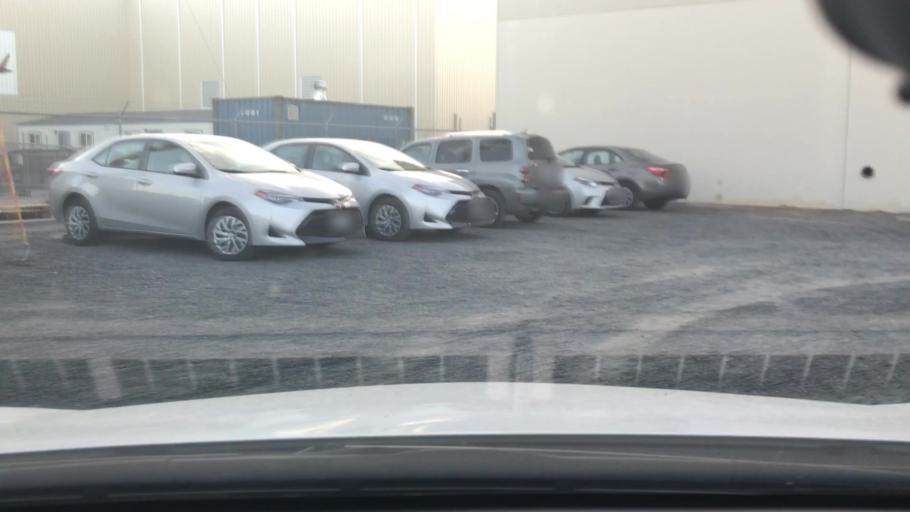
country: US
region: Washington
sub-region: Grant County
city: Moses Lake North
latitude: 47.1889
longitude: -119.3199
